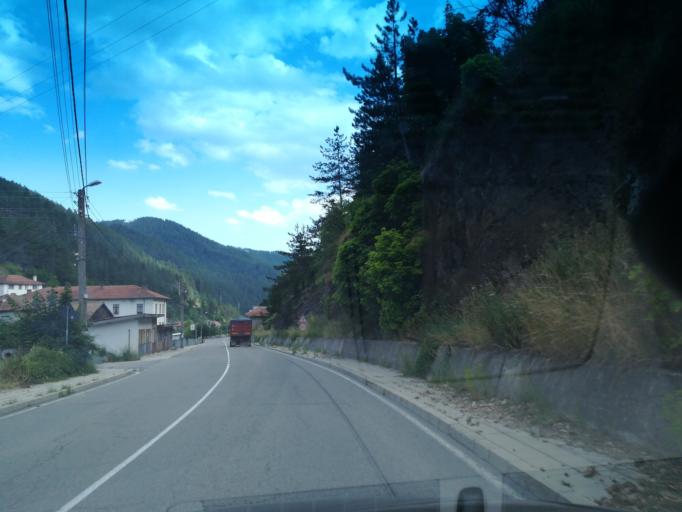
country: BG
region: Smolyan
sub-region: Obshtina Smolyan
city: Smolyan
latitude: 41.6539
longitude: 24.7584
